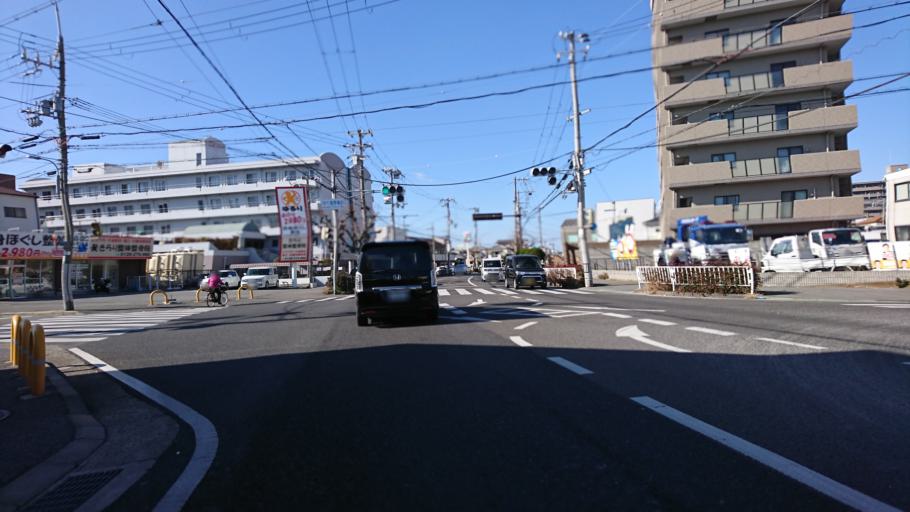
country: JP
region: Hyogo
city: Akashi
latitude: 34.6483
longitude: 134.9773
